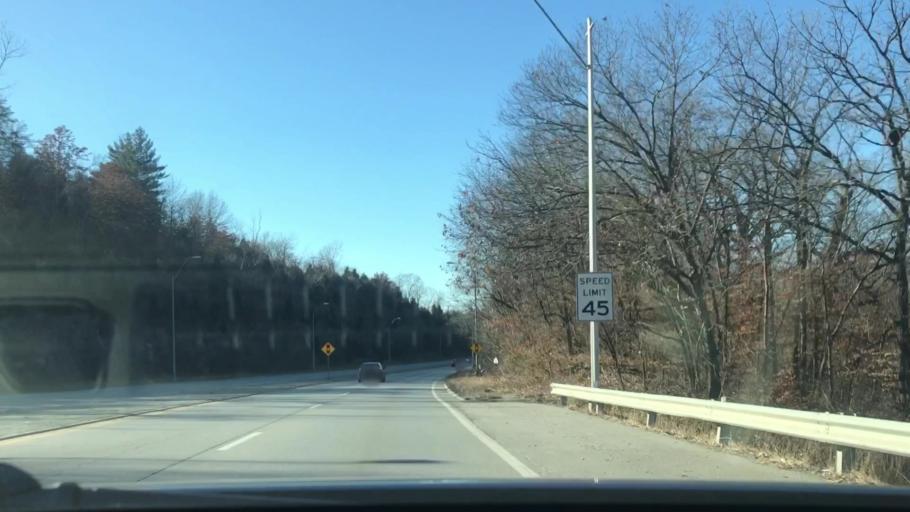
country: US
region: Missouri
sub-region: Jackson County
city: Sugar Creek
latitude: 39.0812
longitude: -94.4829
